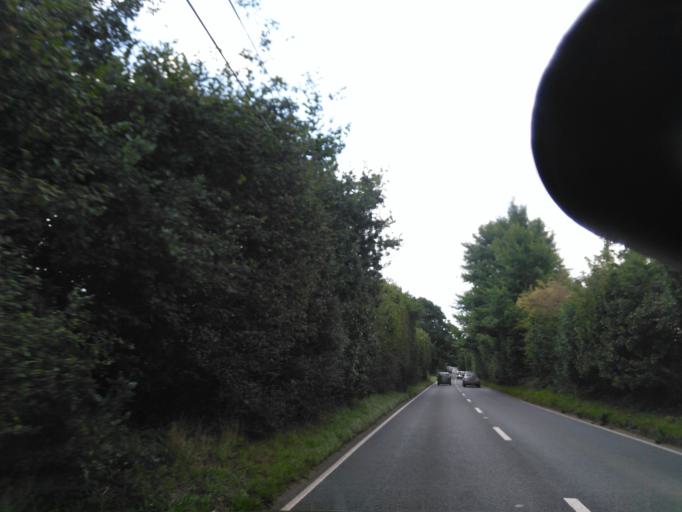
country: GB
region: England
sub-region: Dorset
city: Lytchett Matravers
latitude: 50.7746
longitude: -2.0689
